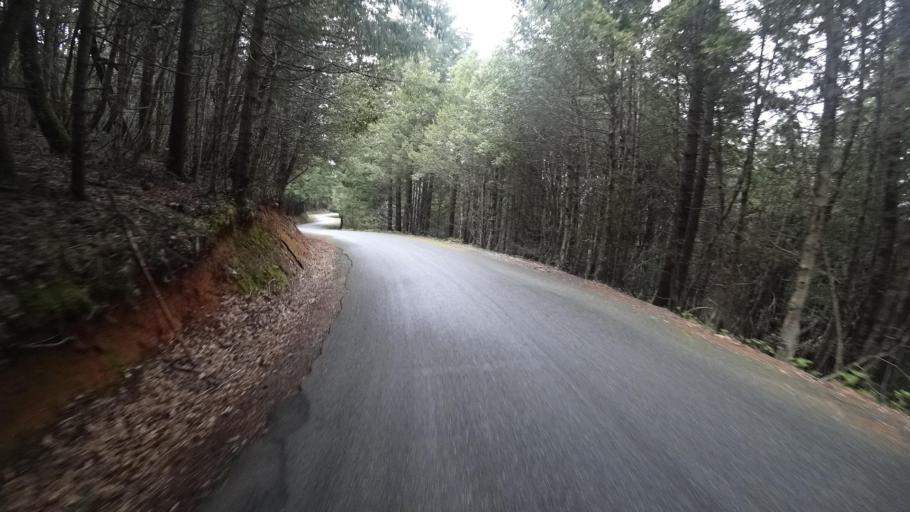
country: US
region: California
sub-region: Humboldt County
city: Willow Creek
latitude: 41.2016
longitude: -123.7822
